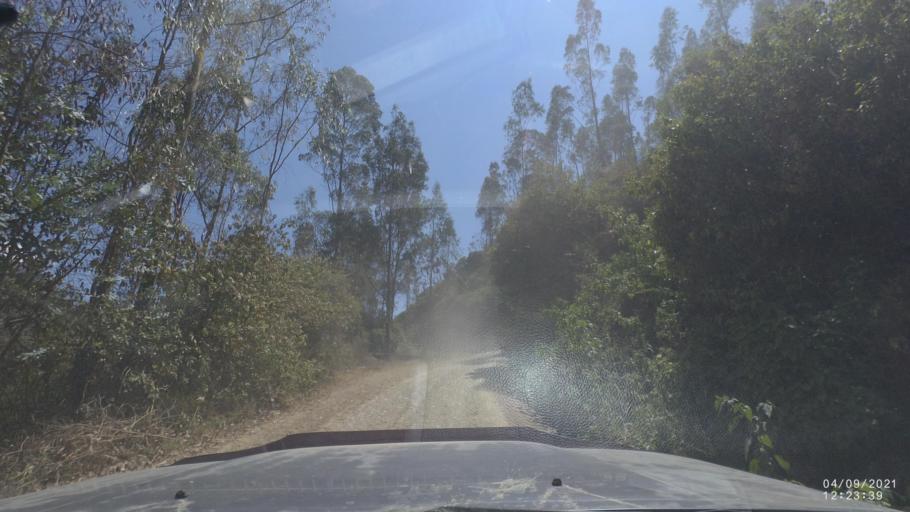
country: BO
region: Cochabamba
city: Colchani
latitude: -17.2378
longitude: -66.5251
